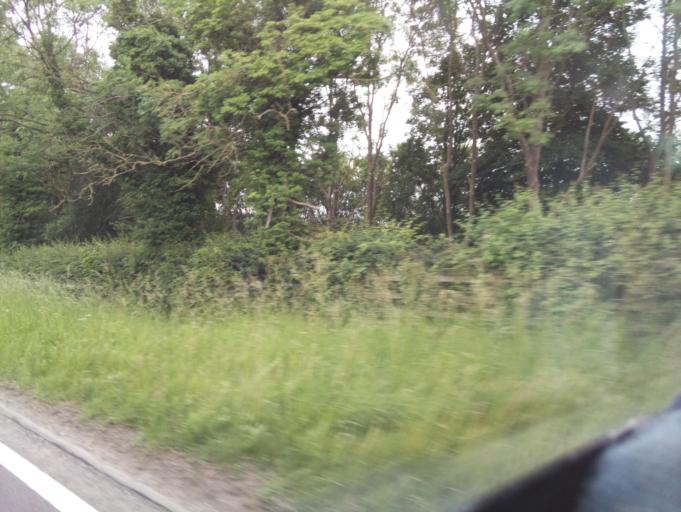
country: GB
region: England
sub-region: District of Rutland
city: Empingham
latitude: 52.6658
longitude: -0.6153
